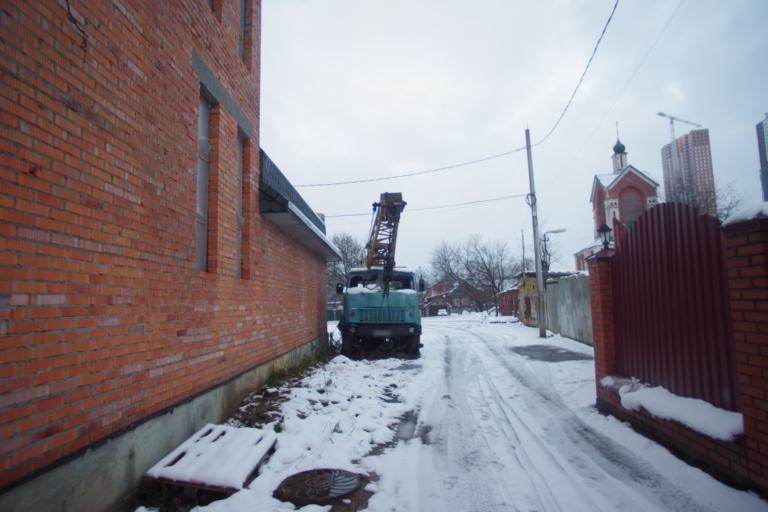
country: RU
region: Moskovskaya
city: Pavshino
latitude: 55.8102
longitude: 37.3557
